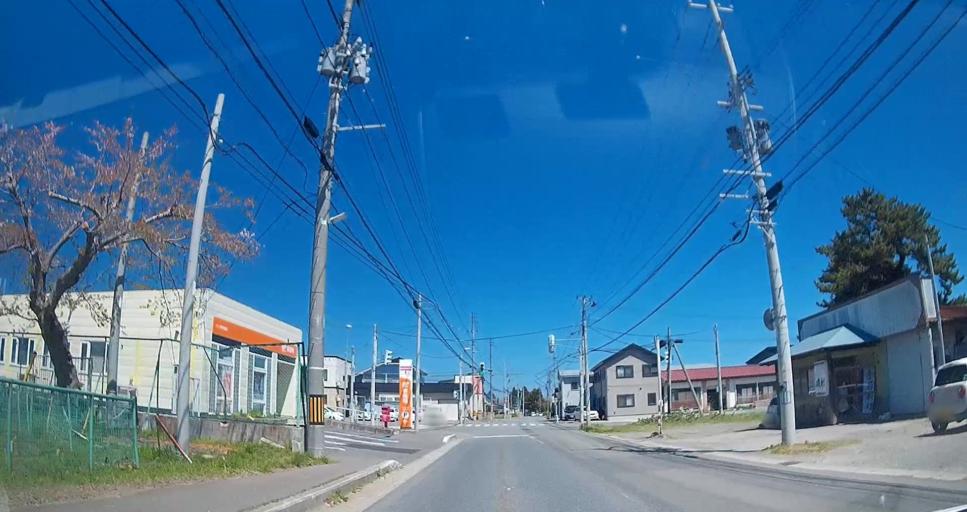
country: JP
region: Aomori
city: Misawa
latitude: 40.9682
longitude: 141.3749
